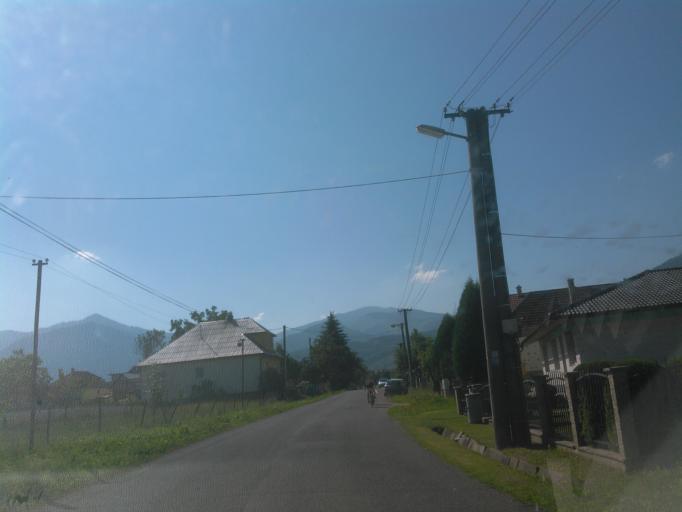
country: SK
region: Zilinsky
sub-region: Okres Liptovsky Mikulas
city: Liptovsky Mikulas
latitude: 49.0361
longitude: 19.5012
